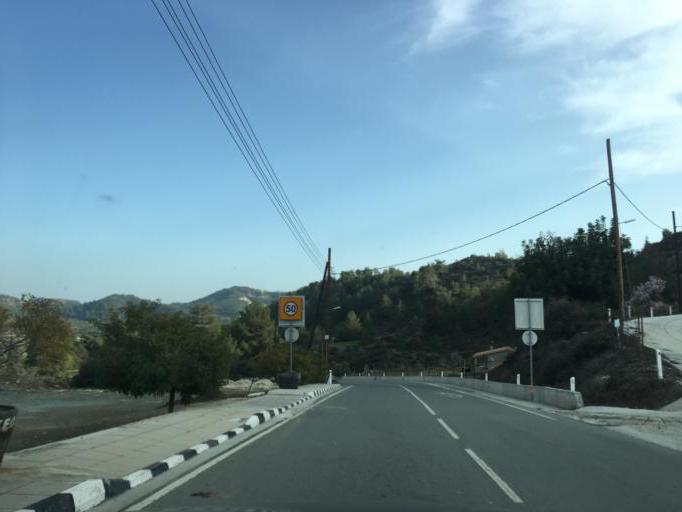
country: CY
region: Limassol
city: Pelendri
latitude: 34.8319
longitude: 32.9581
